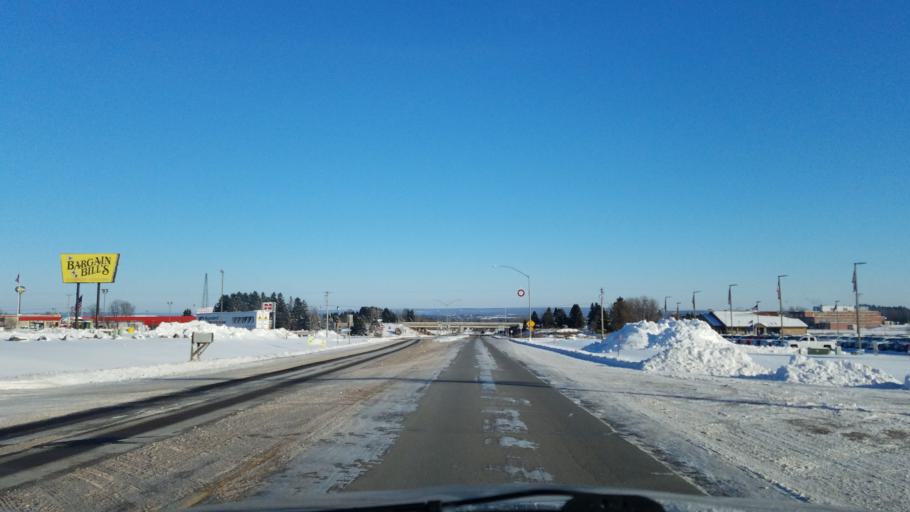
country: US
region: Wisconsin
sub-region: Barron County
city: Rice Lake
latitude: 45.5094
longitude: -91.7674
